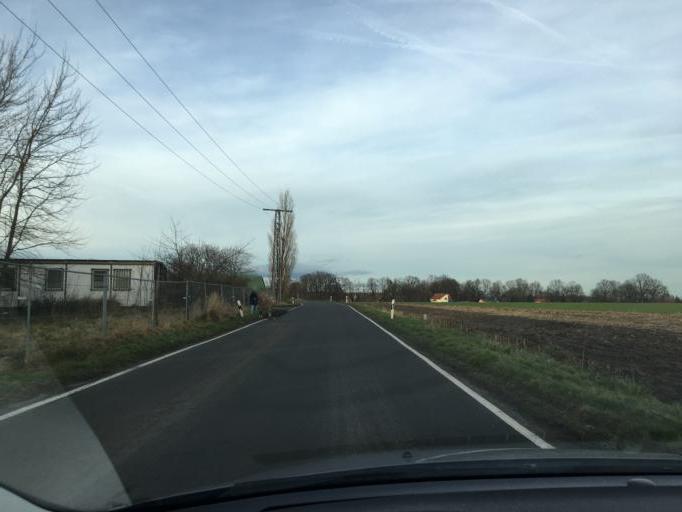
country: DE
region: Saxony
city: Belgershain
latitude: 51.2119
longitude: 12.5244
